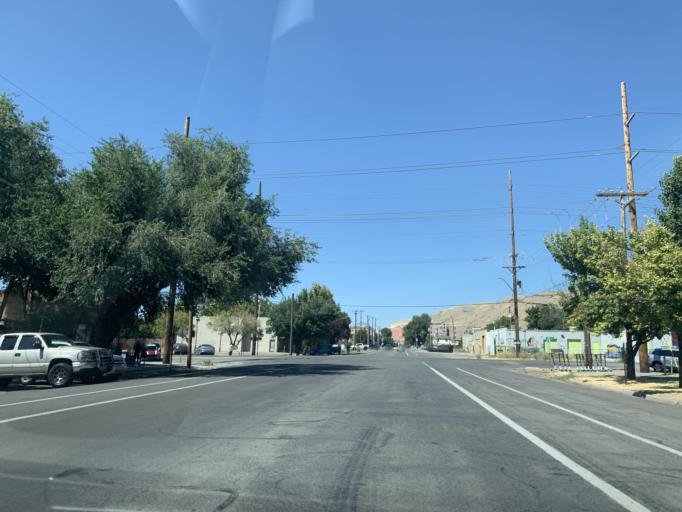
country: US
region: Utah
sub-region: Salt Lake County
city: Salt Lake City
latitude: 40.7667
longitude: -111.9082
